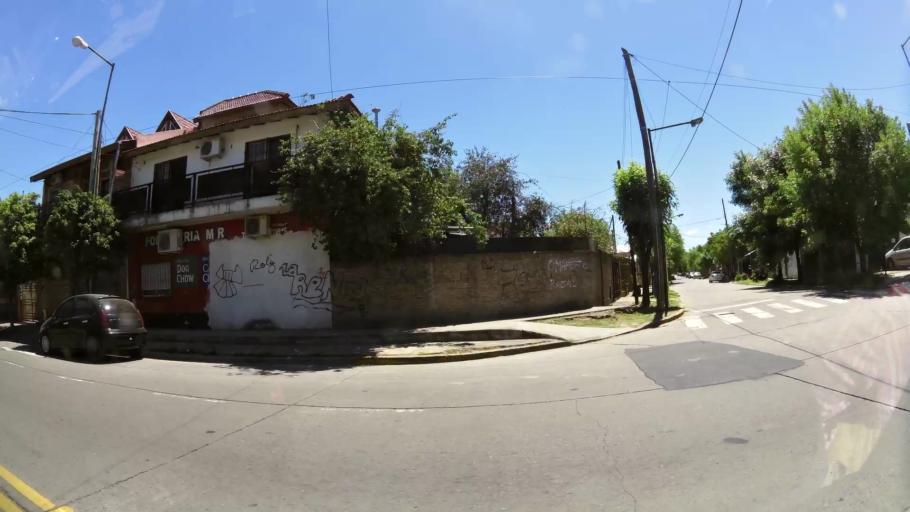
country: AR
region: Buenos Aires
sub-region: Partido de Tigre
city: Tigre
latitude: -34.5005
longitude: -58.5835
